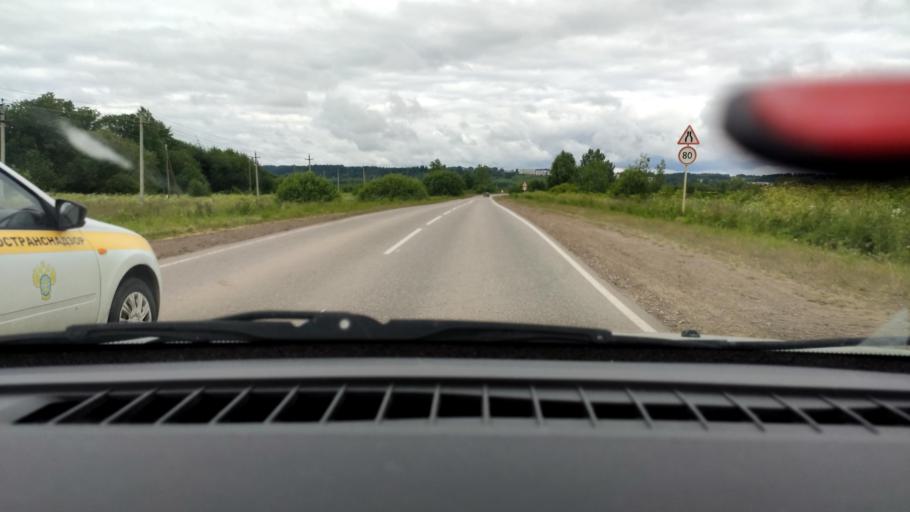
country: RU
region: Perm
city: Chaykovskaya
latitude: 58.0929
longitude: 55.6022
